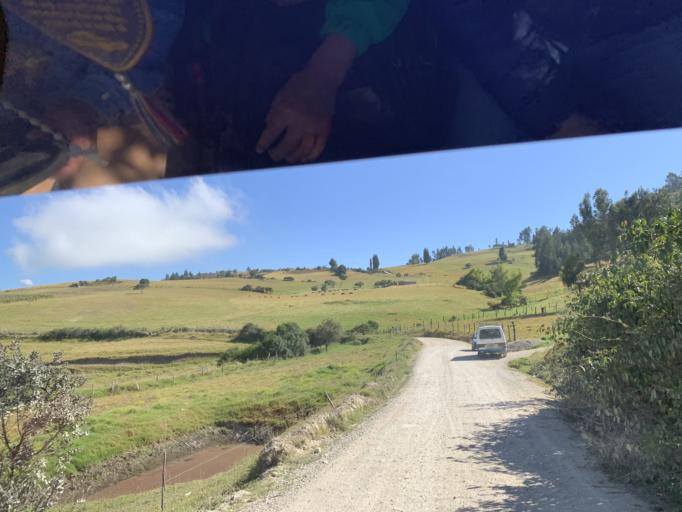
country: CO
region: Boyaca
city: Tuta
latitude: 5.6922
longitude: -73.1459
